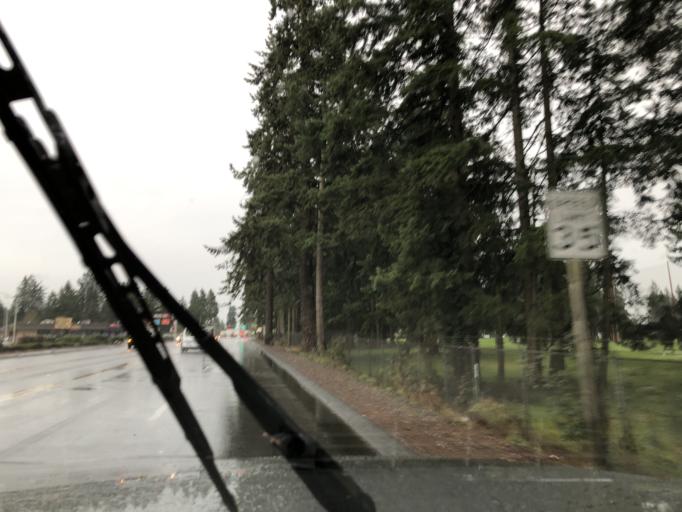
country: US
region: Washington
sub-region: Pierce County
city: Spanaway
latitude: 47.1204
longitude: -122.4382
